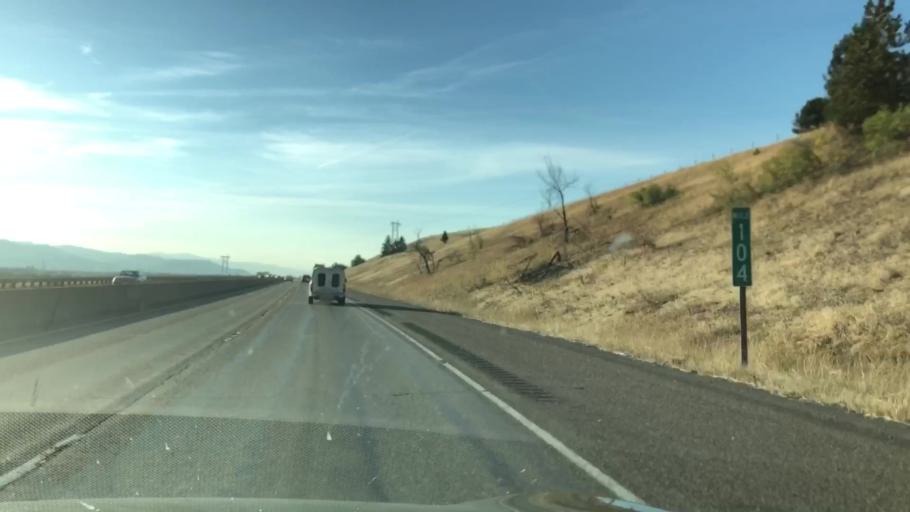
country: US
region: Montana
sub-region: Missoula County
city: Missoula
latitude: 46.8900
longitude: -113.9999
